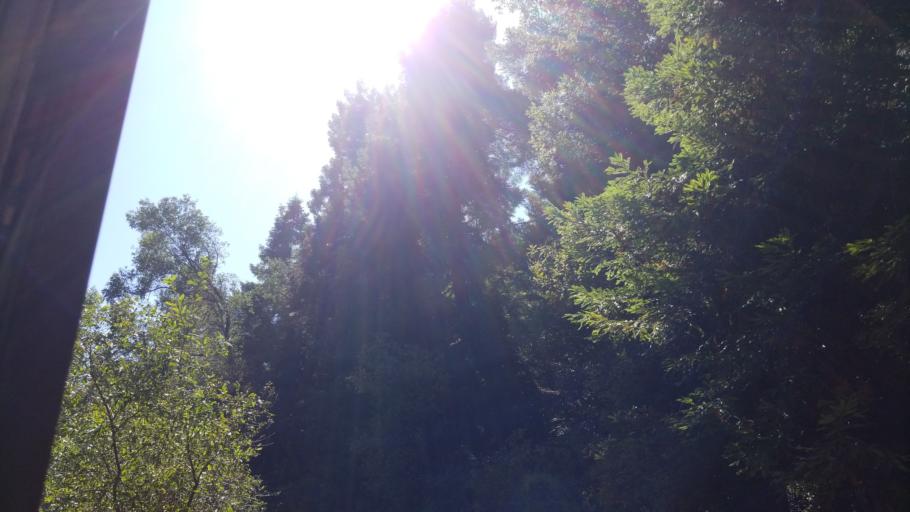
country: US
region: California
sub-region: Mendocino County
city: Fort Bragg
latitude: 39.4490
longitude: -123.7827
